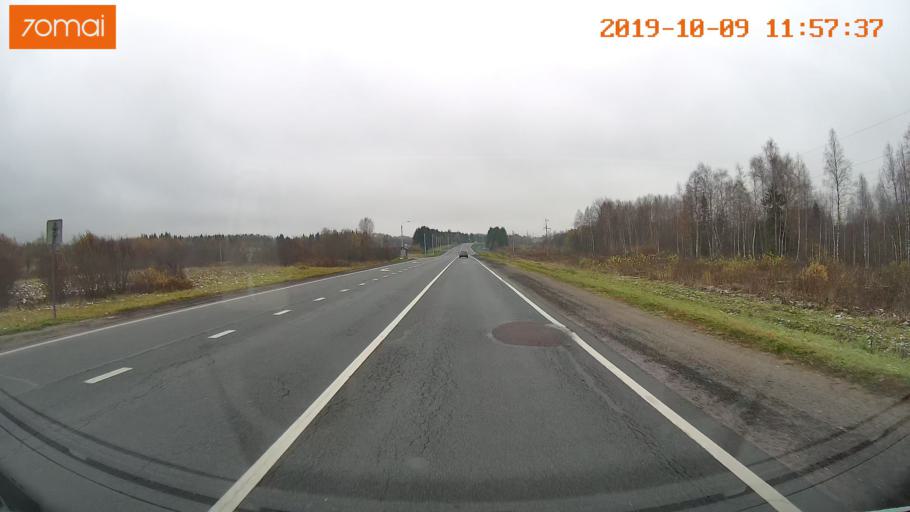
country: RU
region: Vologda
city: Gryazovets
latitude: 58.7298
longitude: 40.2936
